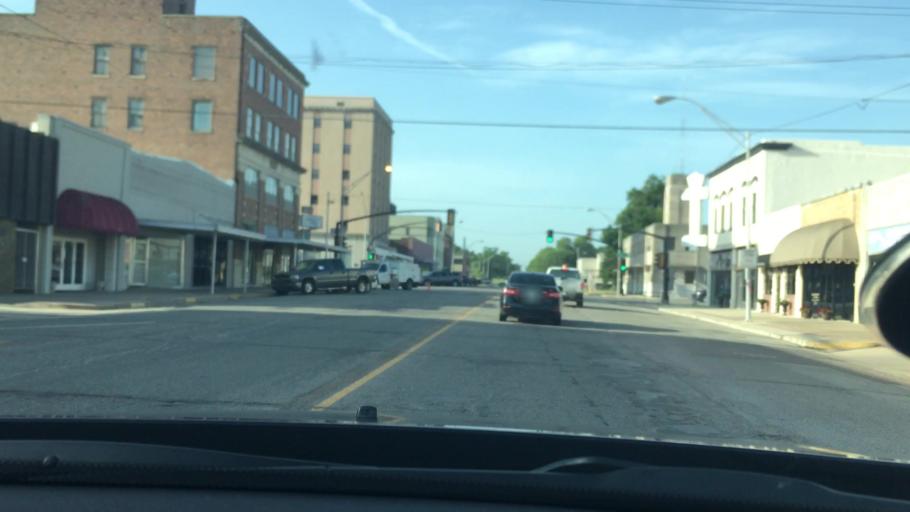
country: US
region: Oklahoma
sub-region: Pontotoc County
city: Ada
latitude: 34.7742
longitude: -96.6787
